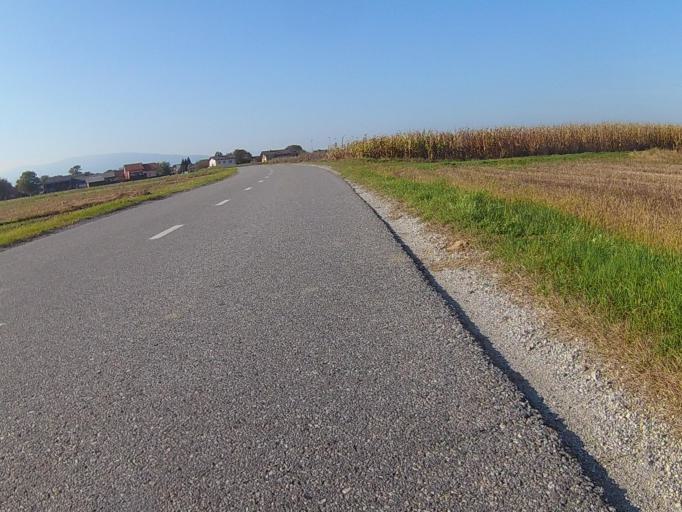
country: SI
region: Starse
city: Starse
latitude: 46.4470
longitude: 15.7533
